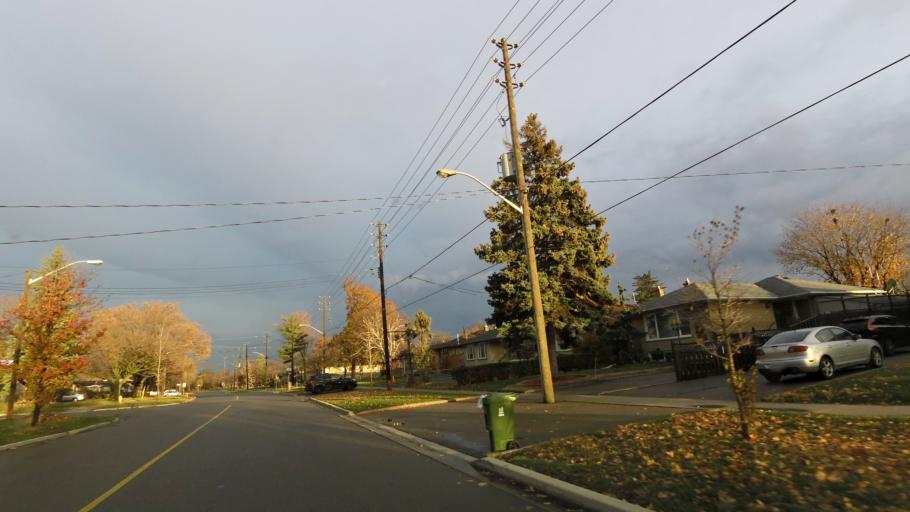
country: CA
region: Ontario
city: Etobicoke
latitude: 43.6618
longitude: -79.5783
